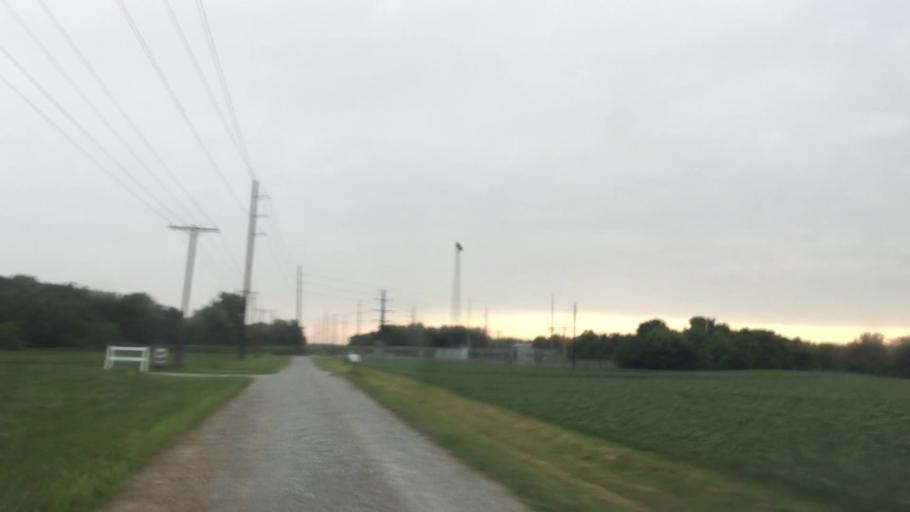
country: US
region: Iowa
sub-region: Lee County
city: Fort Madison
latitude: 40.6044
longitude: -91.2675
